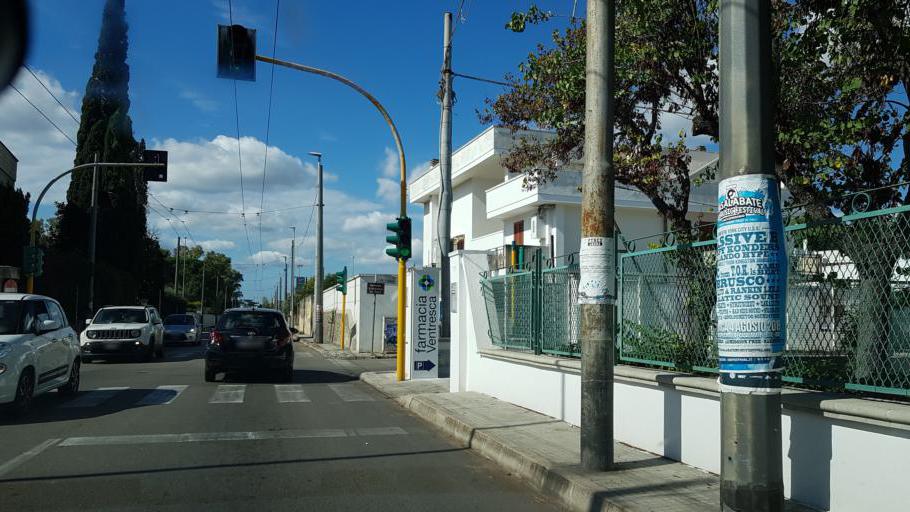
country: IT
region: Apulia
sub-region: Provincia di Lecce
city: Lecce
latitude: 40.3442
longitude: 18.1449
